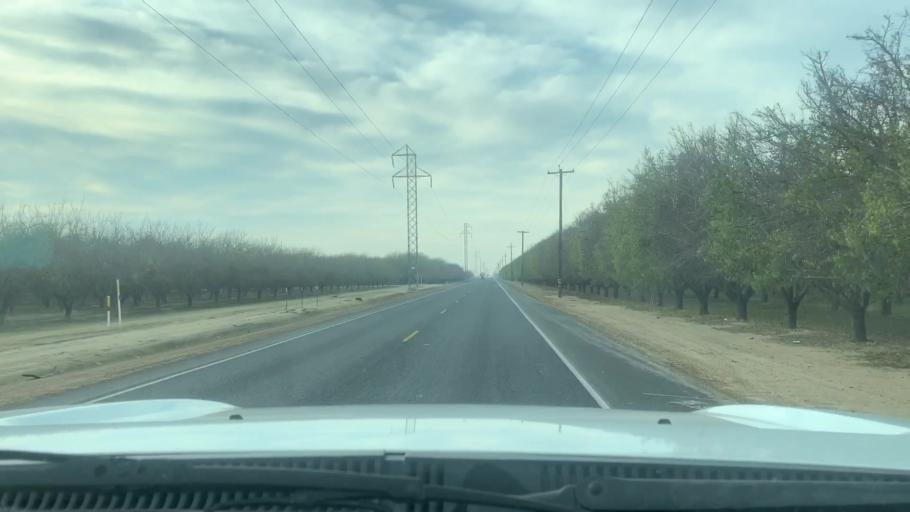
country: US
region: California
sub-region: Kern County
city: Shafter
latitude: 35.4418
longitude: -119.2988
